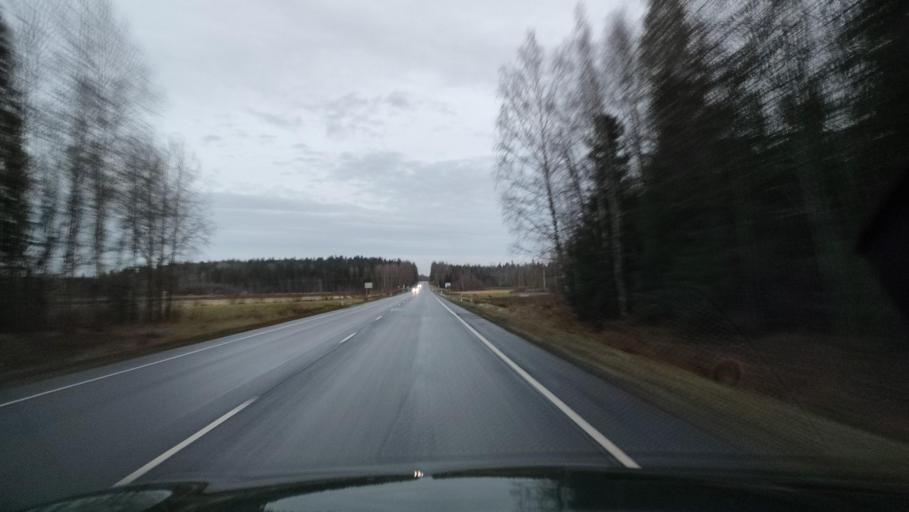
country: FI
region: Ostrobothnia
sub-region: Vaasa
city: Ristinummi
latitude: 62.9906
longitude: 21.7666
